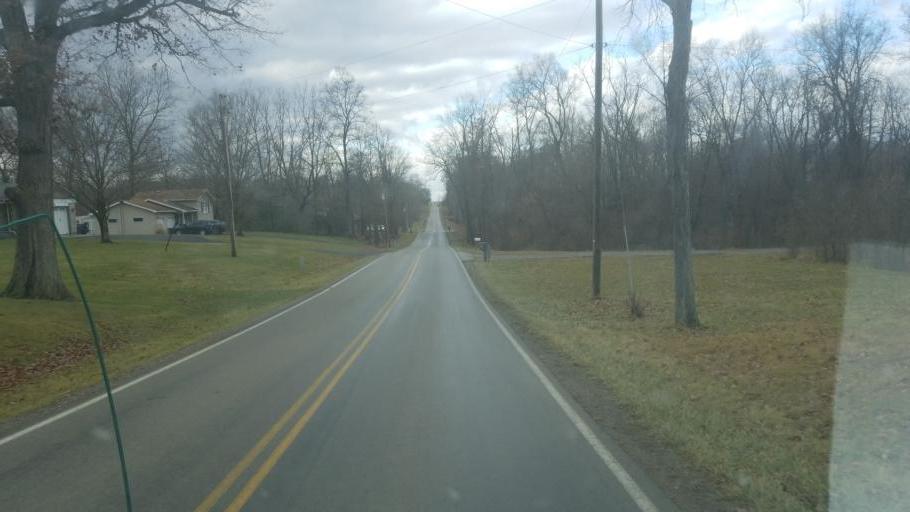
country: US
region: Ohio
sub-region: Wyandot County
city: Upper Sandusky
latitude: 40.7748
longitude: -83.2244
